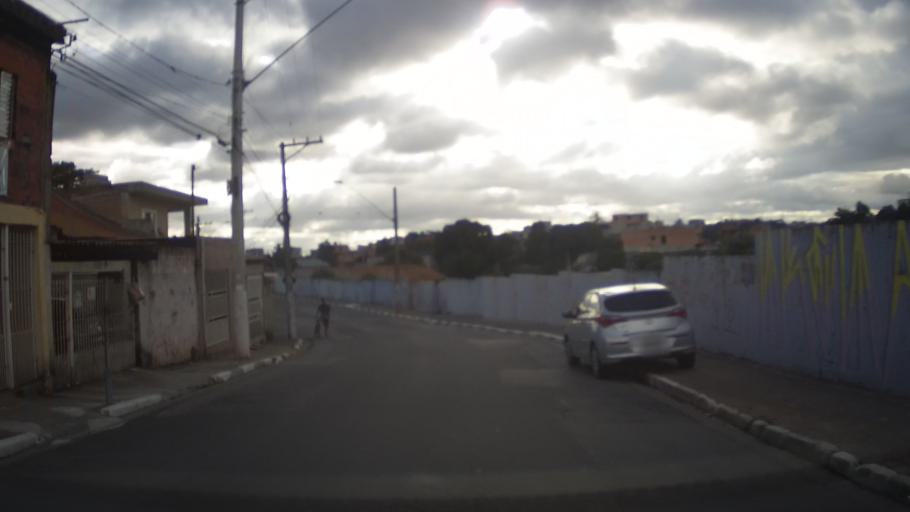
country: BR
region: Sao Paulo
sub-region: Itaquaquecetuba
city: Itaquaquecetuba
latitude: -23.4615
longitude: -46.4117
